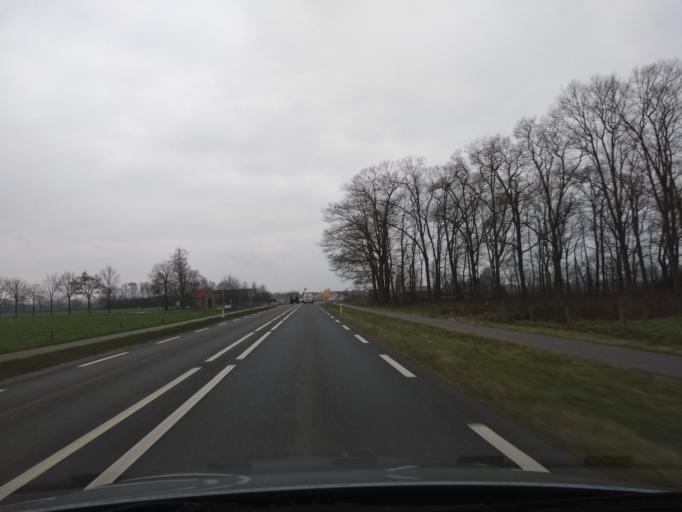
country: NL
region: Overijssel
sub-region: Gemeente Haaksbergen
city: Haaksbergen
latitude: 52.1862
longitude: 6.7377
